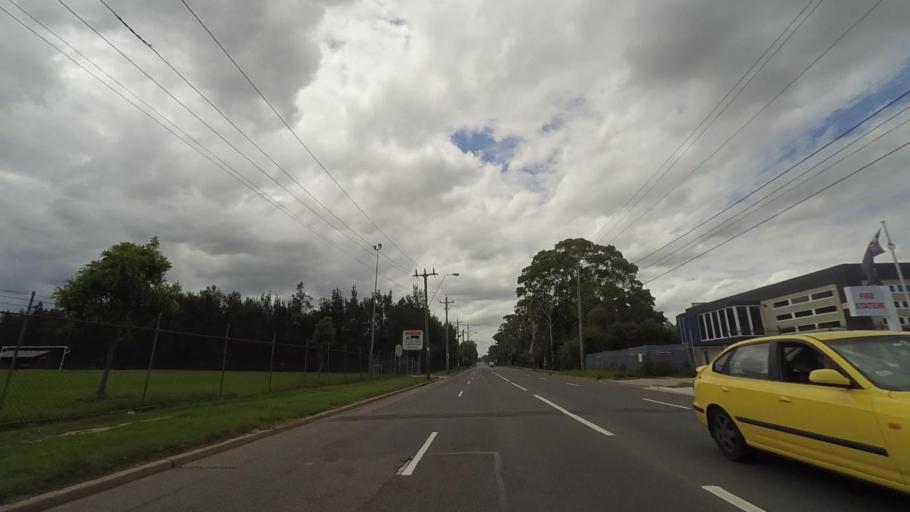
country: AU
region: New South Wales
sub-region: Fairfield
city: Fairfield East
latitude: -33.8588
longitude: 150.9583
